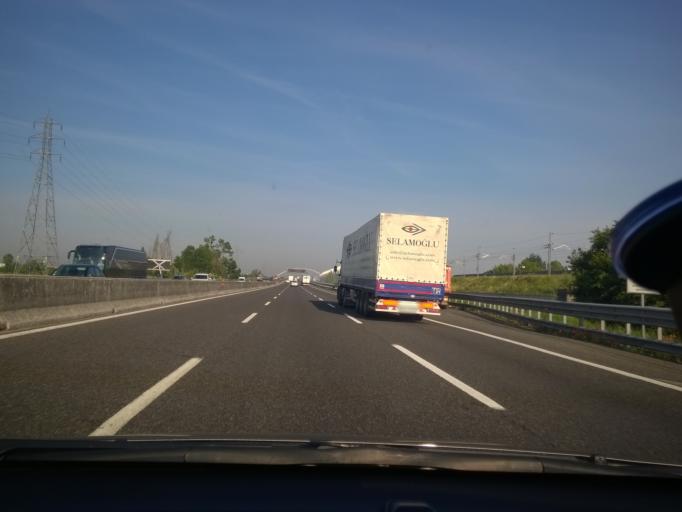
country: IT
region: Emilia-Romagna
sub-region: Provincia di Reggio Emilia
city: Reggio nell'Emilia
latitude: 44.7226
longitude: 10.6606
